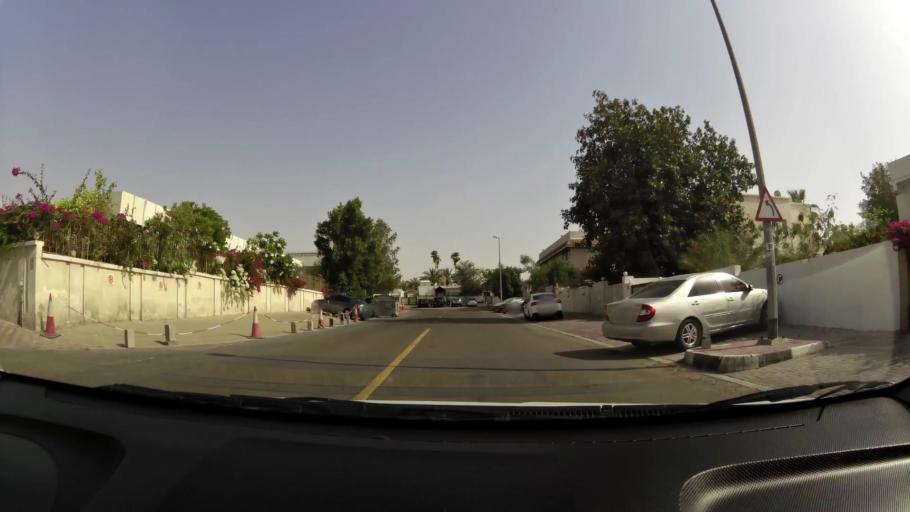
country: AE
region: Ash Shariqah
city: Sharjah
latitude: 25.2432
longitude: 55.3508
